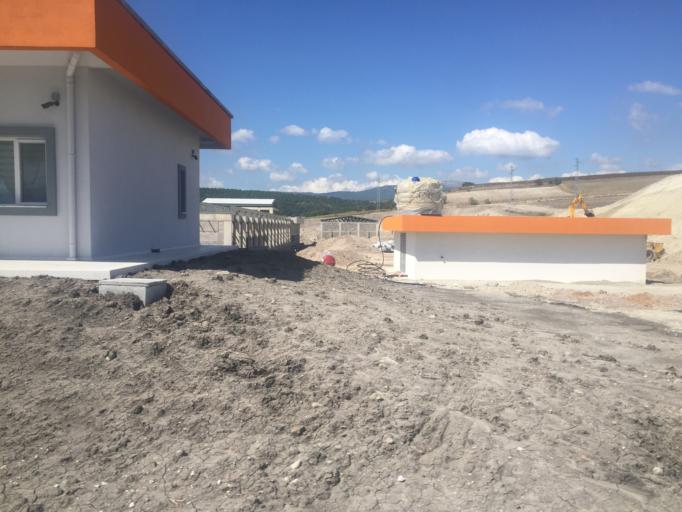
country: TR
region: Balikesir
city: Susurluk
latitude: 39.9619
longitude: 28.1647
